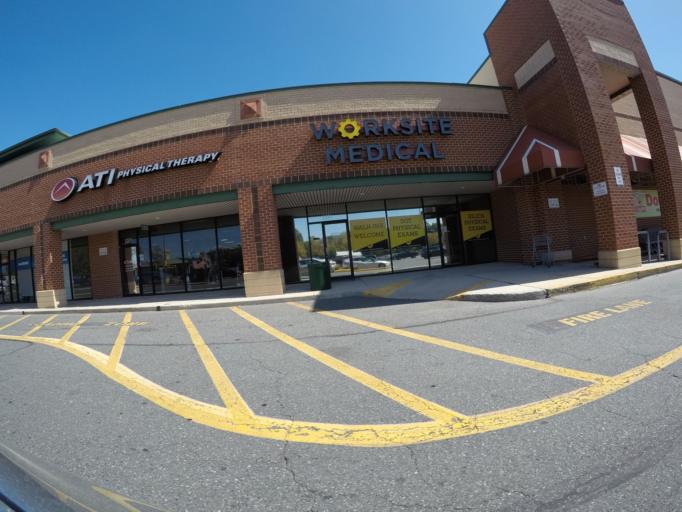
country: US
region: Maryland
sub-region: Harford County
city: Riverside
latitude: 39.4805
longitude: -76.2480
